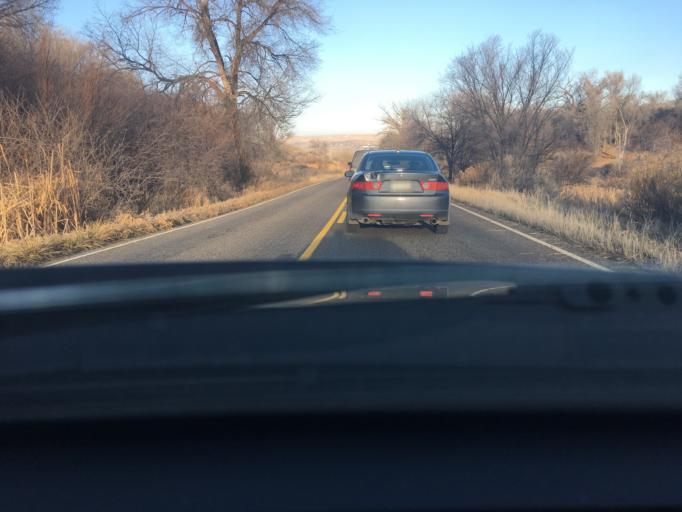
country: US
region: Colorado
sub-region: Delta County
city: Delta
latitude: 38.7441
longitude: -108.1143
